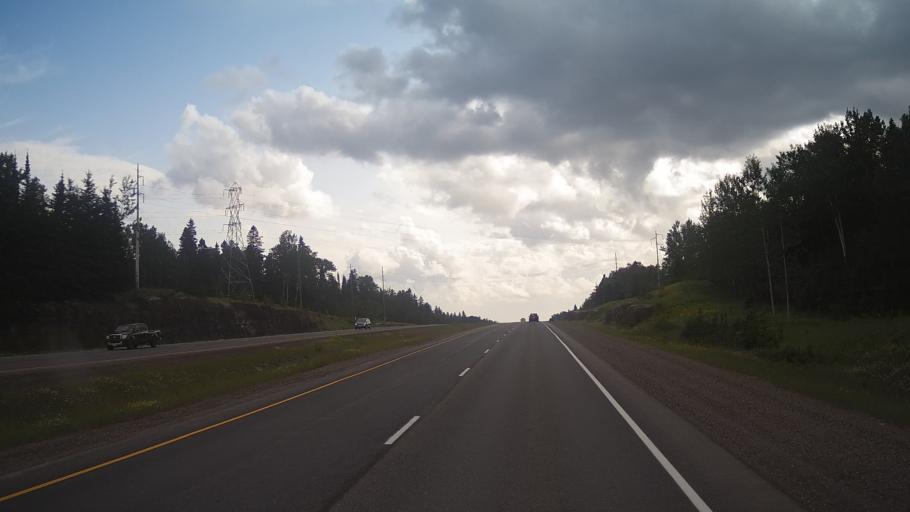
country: CA
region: Ontario
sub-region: Thunder Bay District
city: Thunder Bay
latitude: 48.4761
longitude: -89.2007
